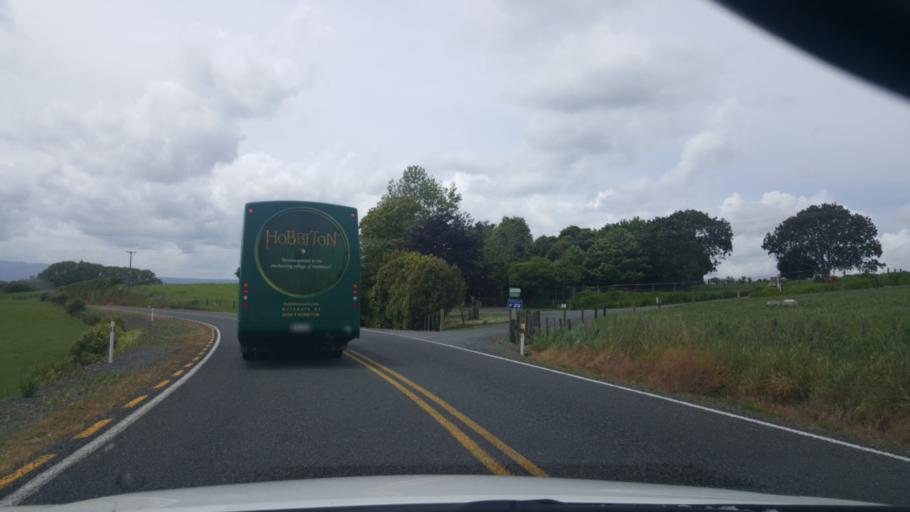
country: NZ
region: Waikato
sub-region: Matamata-Piako District
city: Matamata
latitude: -37.8804
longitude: 175.6968
